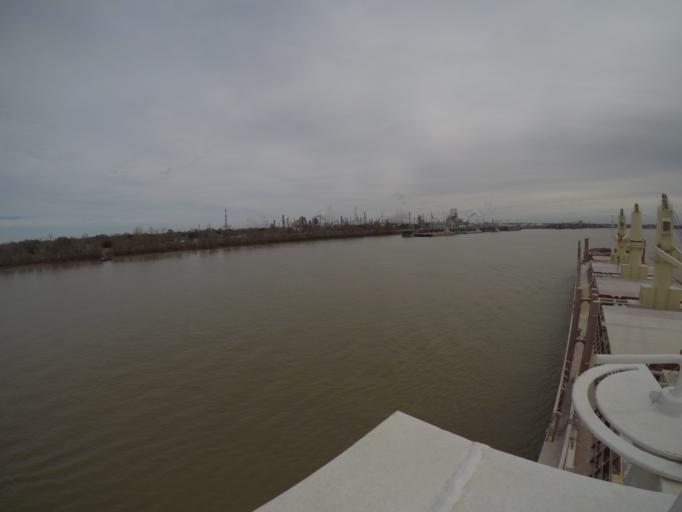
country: US
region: Louisiana
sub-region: Saint Charles Parish
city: Norco
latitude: 29.9940
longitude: -90.4173
